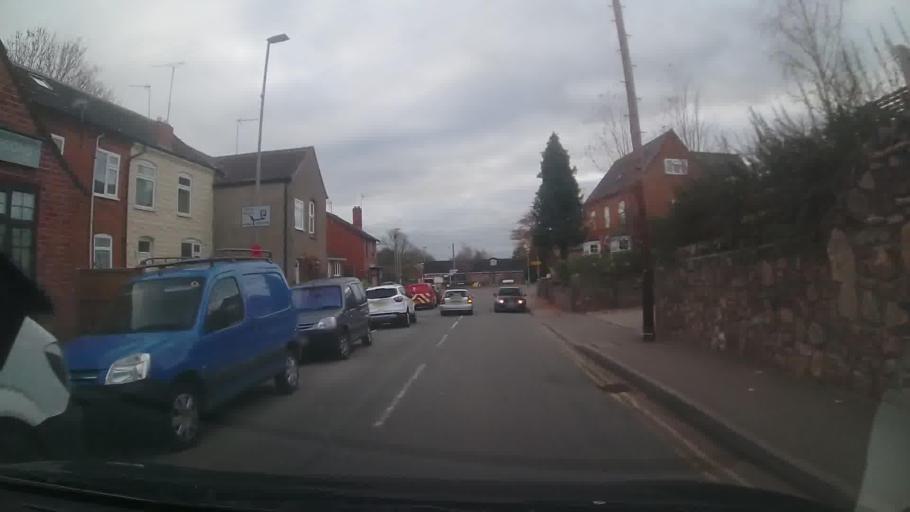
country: GB
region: England
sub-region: Leicestershire
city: Kirby Muxloe
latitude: 52.6477
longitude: -1.2454
